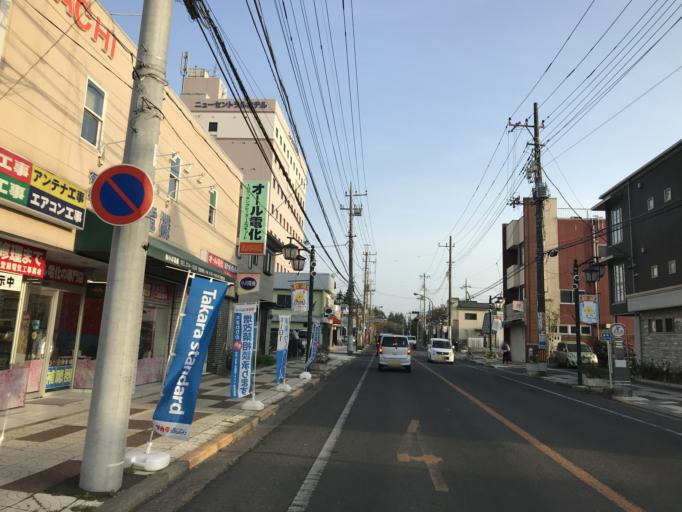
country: JP
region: Ibaraki
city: Katsuta
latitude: 36.3874
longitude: 140.5273
